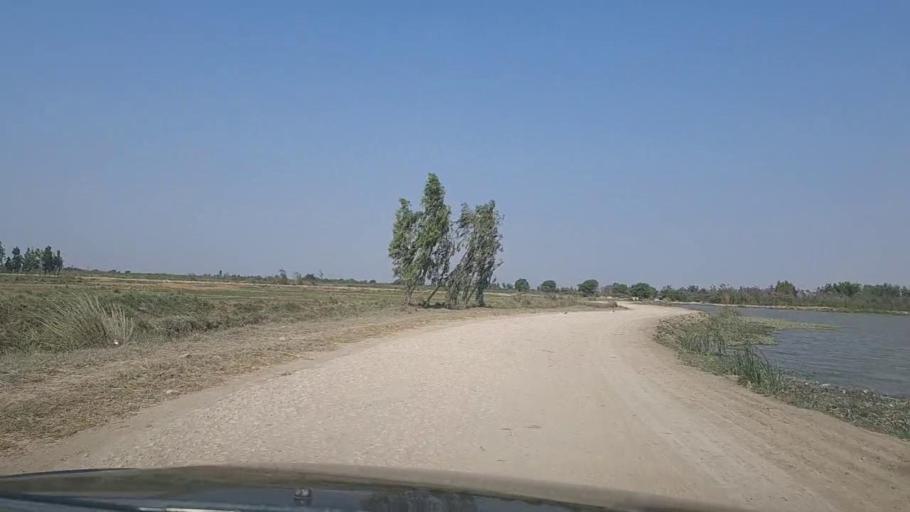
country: PK
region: Sindh
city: Thatta
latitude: 24.6280
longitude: 67.8138
